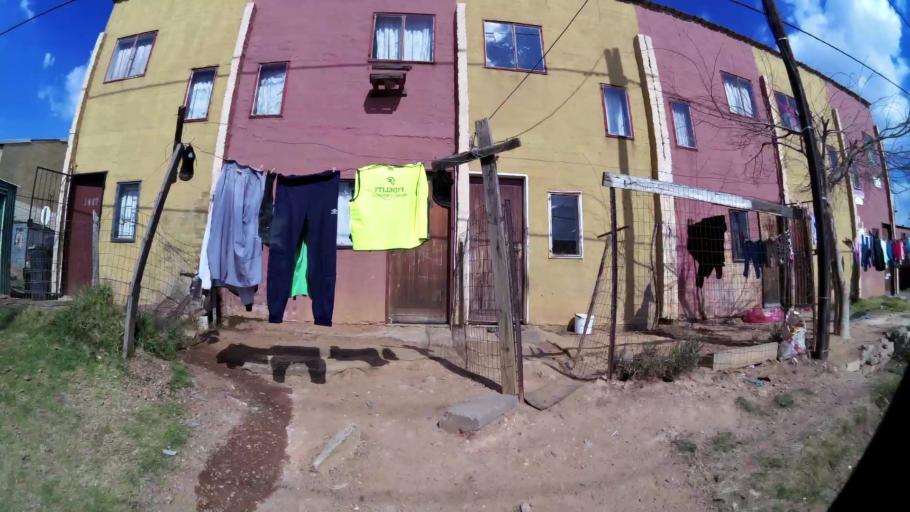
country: ZA
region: Gauteng
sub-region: City of Johannesburg Metropolitan Municipality
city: Roodepoort
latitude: -26.1839
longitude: 27.8434
